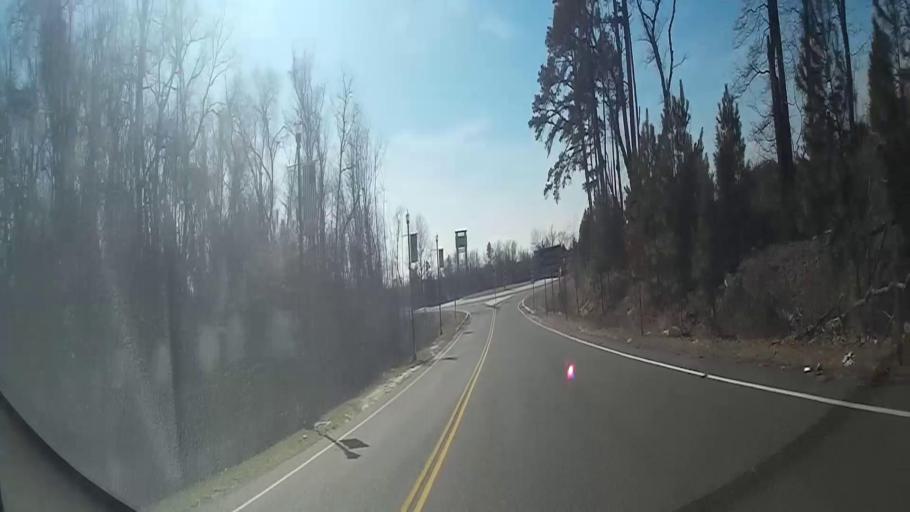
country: US
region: New Jersey
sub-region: Gloucester County
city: Turnersville
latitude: 39.7891
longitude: -75.0459
